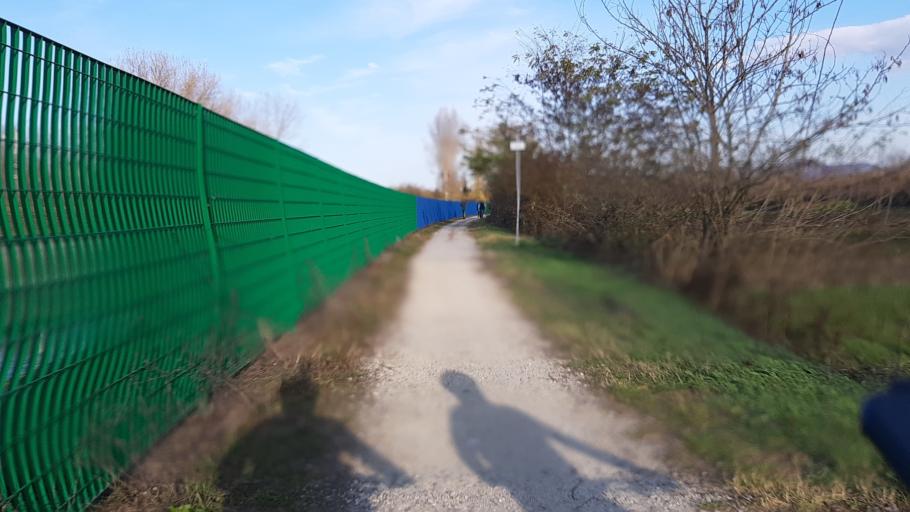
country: IT
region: Piedmont
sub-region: Provincia di Torino
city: San Mauro Torinese
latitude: 45.1205
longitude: 7.7785
